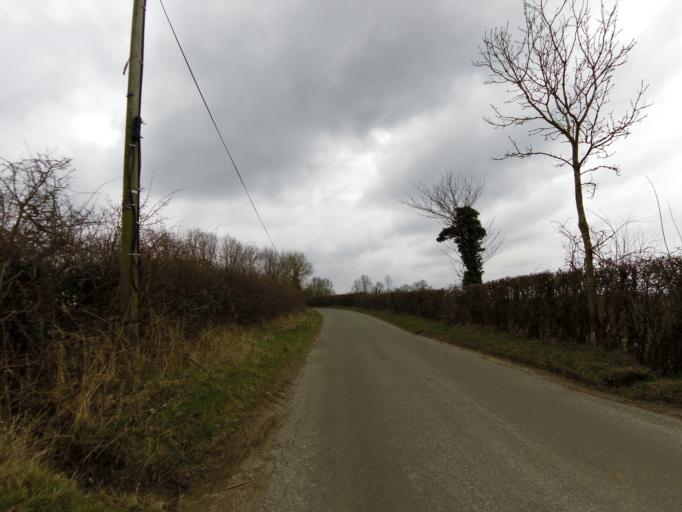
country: GB
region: England
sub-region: Suffolk
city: Halesworth
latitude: 52.3902
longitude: 1.5189
